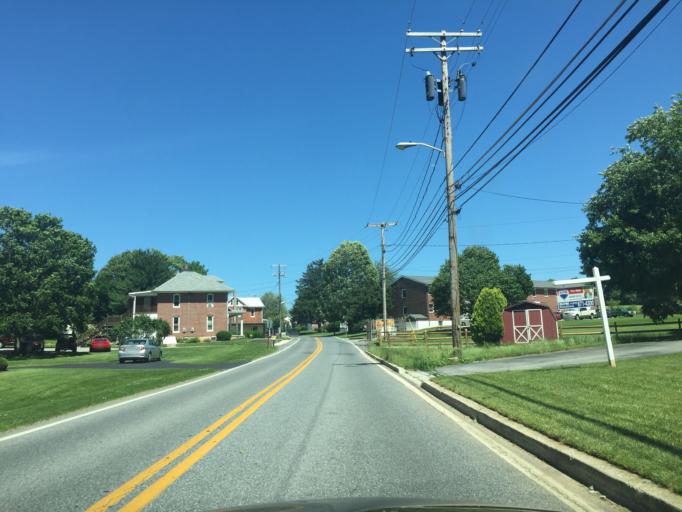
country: US
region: Maryland
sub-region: Carroll County
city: Manchester
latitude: 39.6602
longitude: -76.8887
